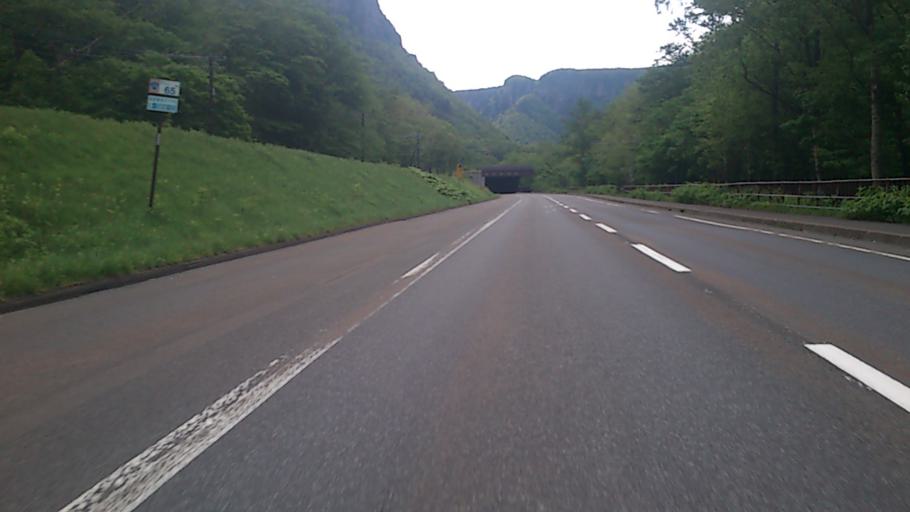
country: JP
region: Hokkaido
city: Kamikawa
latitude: 43.7404
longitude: 142.9371
